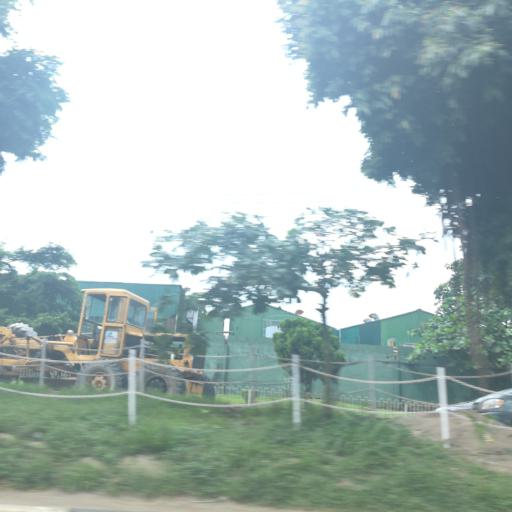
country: NG
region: Lagos
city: Ojota
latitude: 6.6015
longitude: 3.3767
